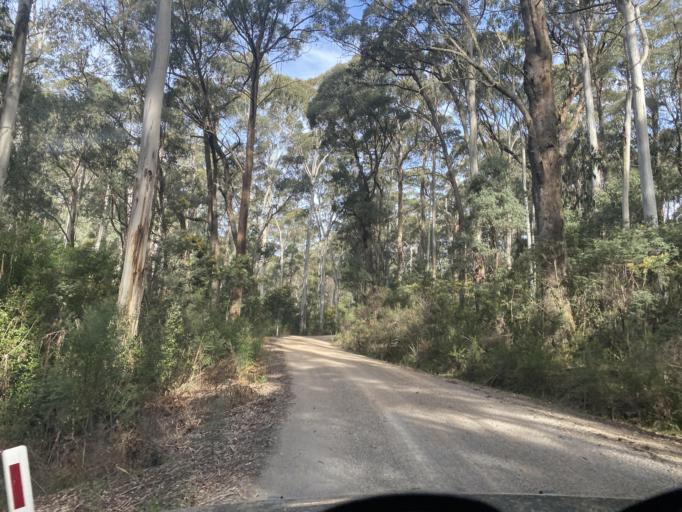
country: AU
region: Victoria
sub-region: Mansfield
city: Mansfield
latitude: -36.8624
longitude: 146.1958
